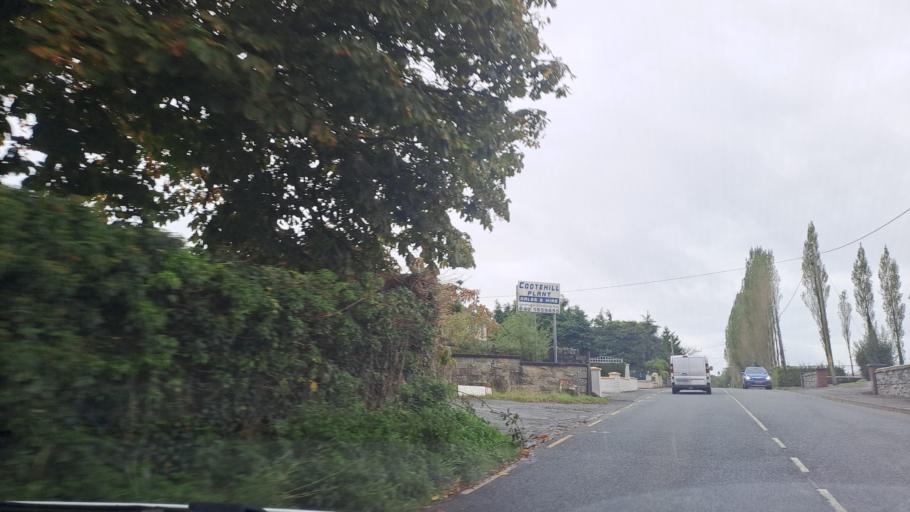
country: IE
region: Ulster
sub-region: An Cabhan
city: Cootehill
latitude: 54.0691
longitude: -7.0656
